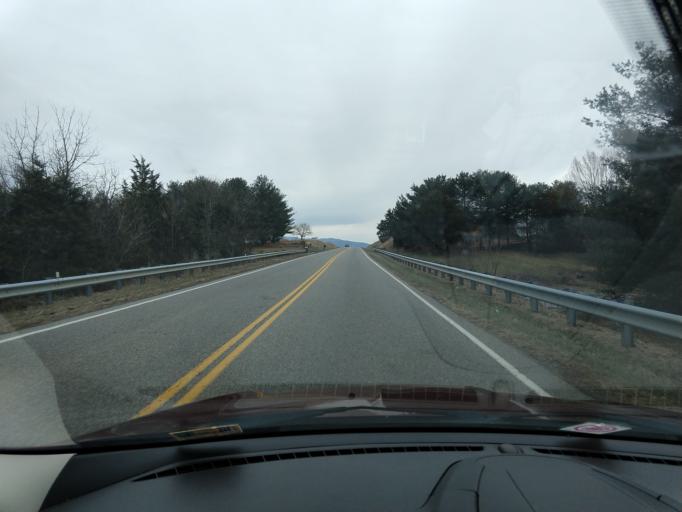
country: US
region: Virginia
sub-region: Augusta County
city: Weyers Cave
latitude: 38.2813
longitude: -78.9039
